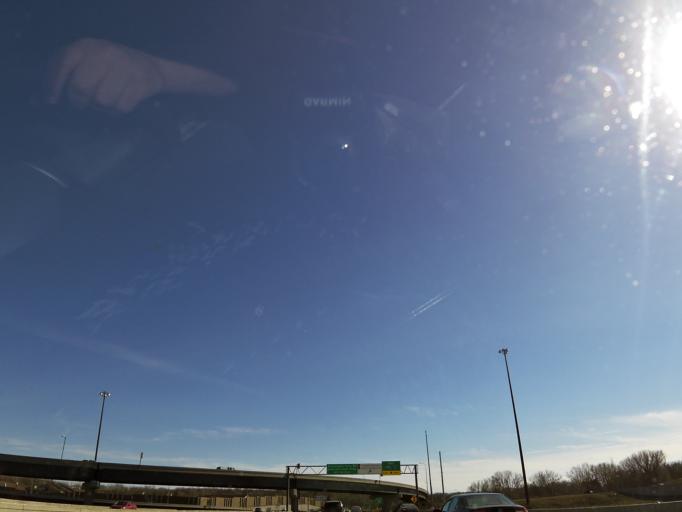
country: US
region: Minnesota
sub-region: Hennepin County
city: Edina
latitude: 44.8600
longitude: -93.3948
